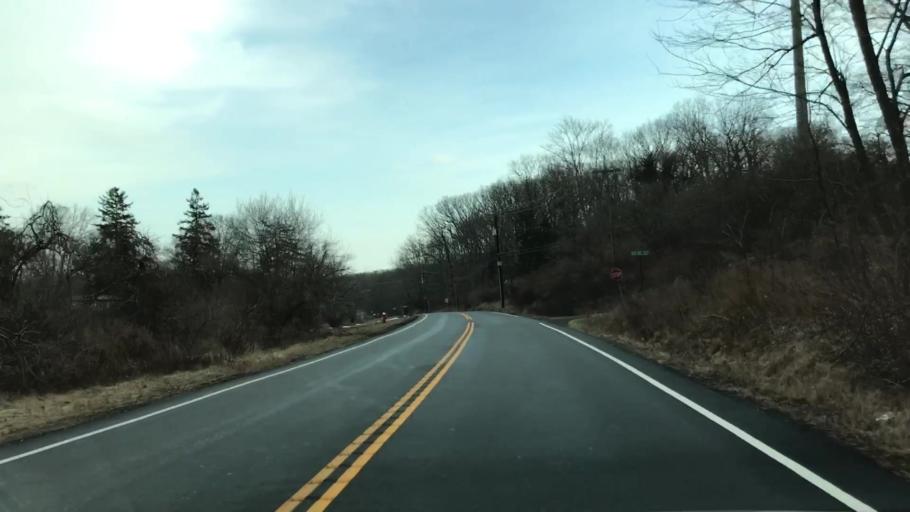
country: US
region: New York
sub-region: Rockland County
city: Wesley Hills
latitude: 41.1795
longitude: -74.0734
